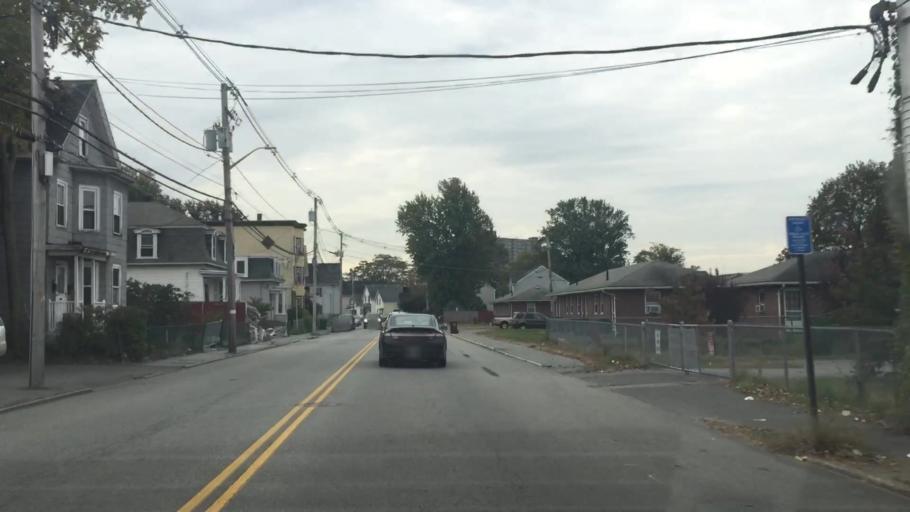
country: US
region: Massachusetts
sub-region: Middlesex County
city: Dracut
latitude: 42.6556
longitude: -71.3124
